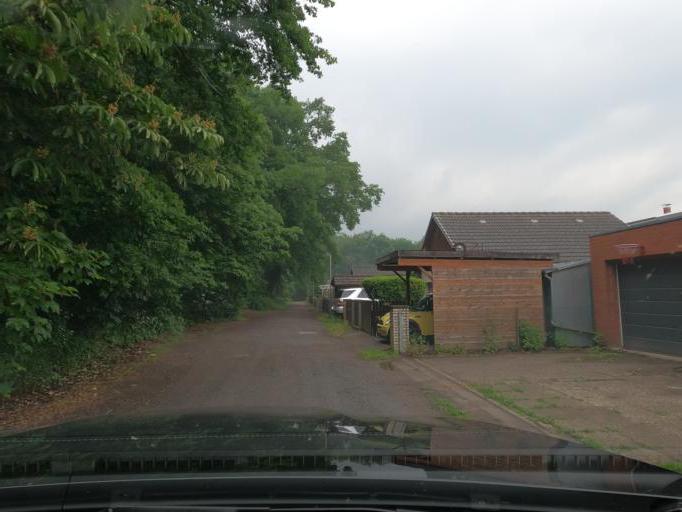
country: DE
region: Lower Saxony
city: Isernhagen Farster Bauerschaft
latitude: 52.3967
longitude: 9.8487
